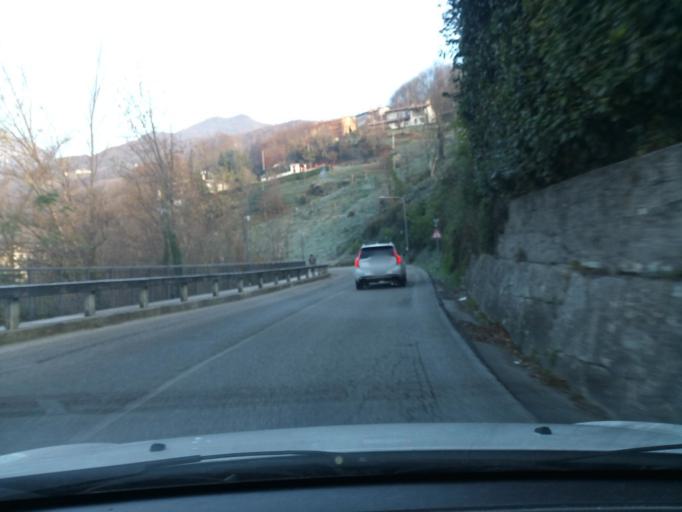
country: IT
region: Veneto
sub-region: Provincia di Vicenza
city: Valli del Pasubio
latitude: 45.7380
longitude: 11.2657
